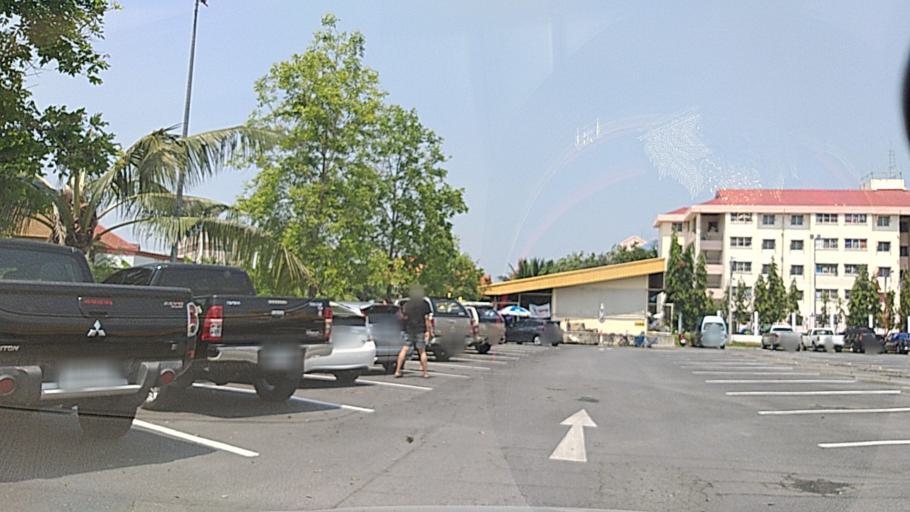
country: TH
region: Bangkok
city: Lak Si
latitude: 13.8726
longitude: 100.5919
